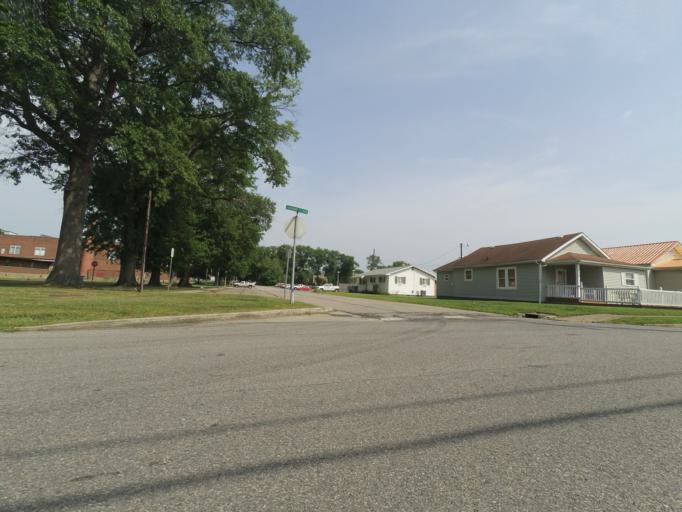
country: US
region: West Virginia
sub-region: Cabell County
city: Huntington
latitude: 38.4102
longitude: -82.4668
